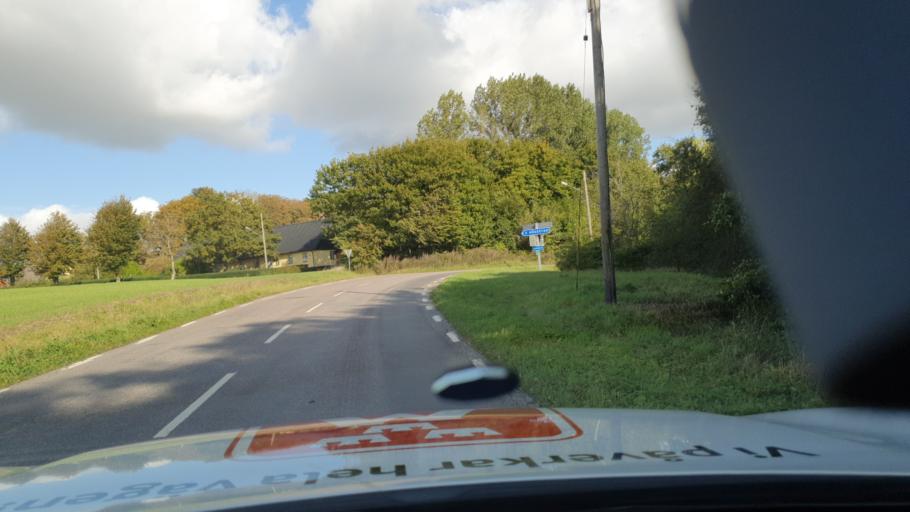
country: SE
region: Skane
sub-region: Ystads Kommun
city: Kopingebro
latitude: 55.5036
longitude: 13.9470
